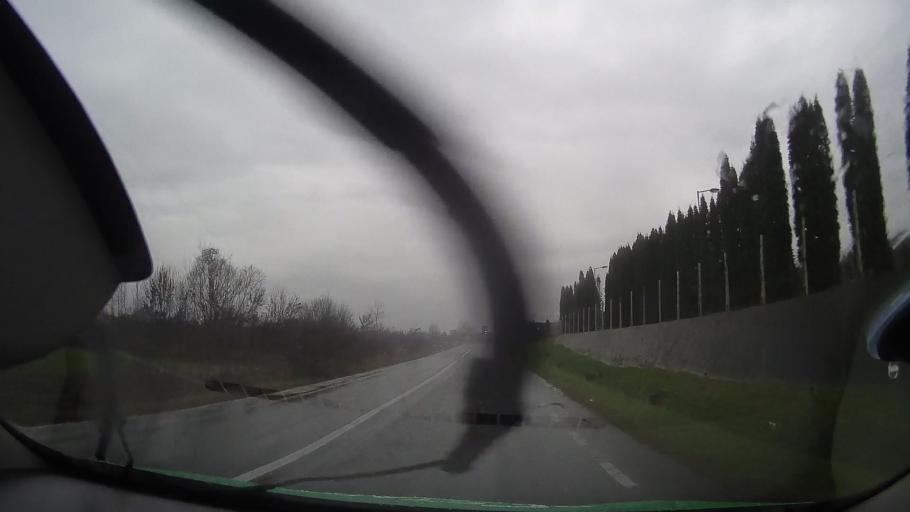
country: RO
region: Bihor
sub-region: Comuna Sambata
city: Sambata
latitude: 46.7885
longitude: 22.2017
